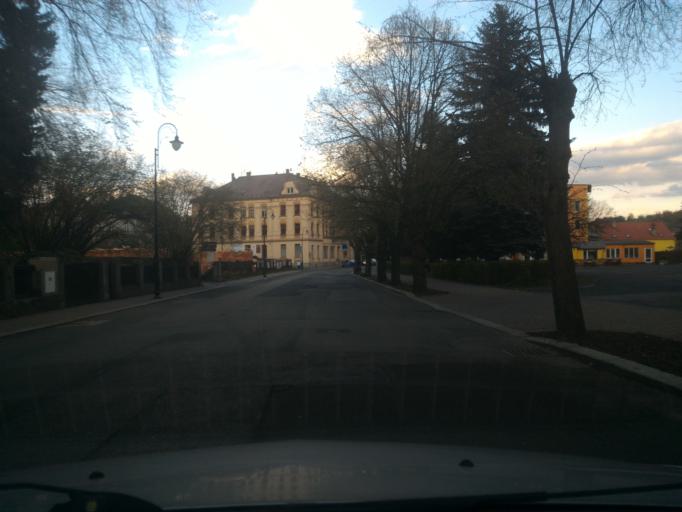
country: CZ
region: Ustecky
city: Varnsdorf
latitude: 50.9088
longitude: 14.6246
